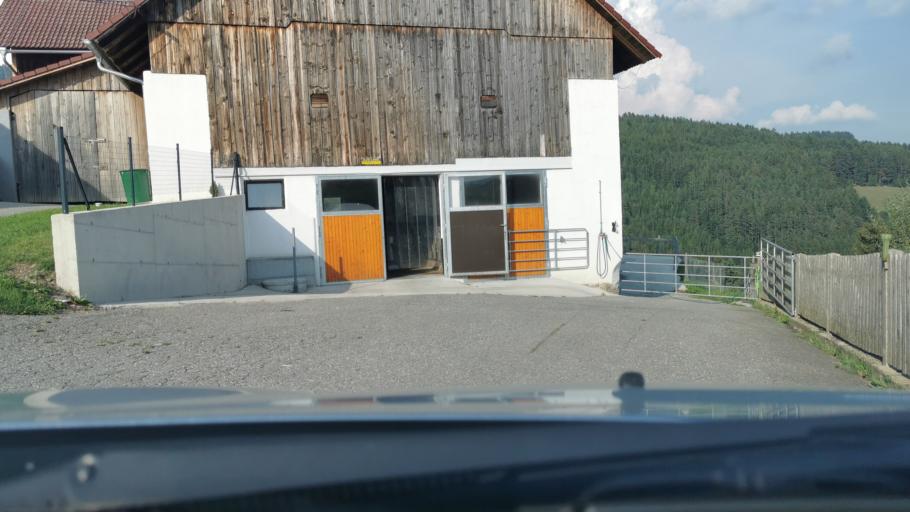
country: AT
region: Styria
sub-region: Politischer Bezirk Weiz
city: Fischbach
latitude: 47.3938
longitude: 15.6528
